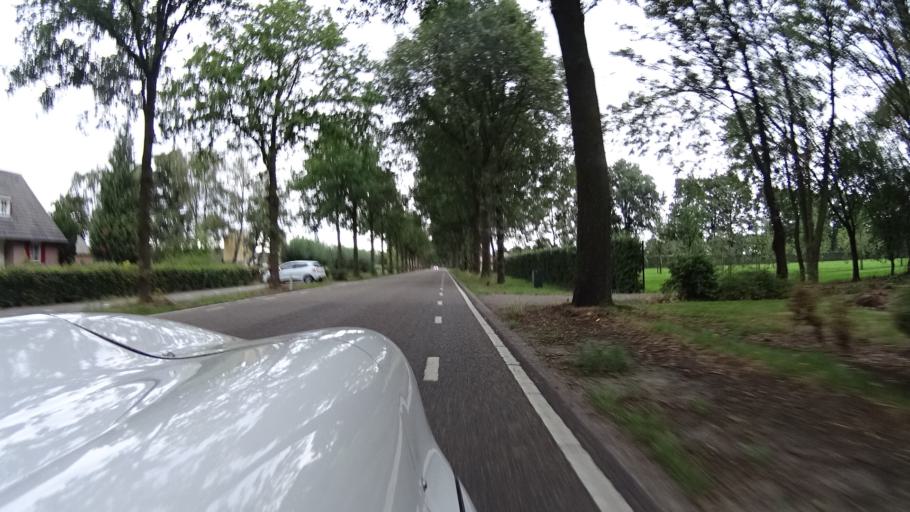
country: NL
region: North Brabant
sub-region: Gemeente Veghel
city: Erp
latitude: 51.6228
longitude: 5.6087
